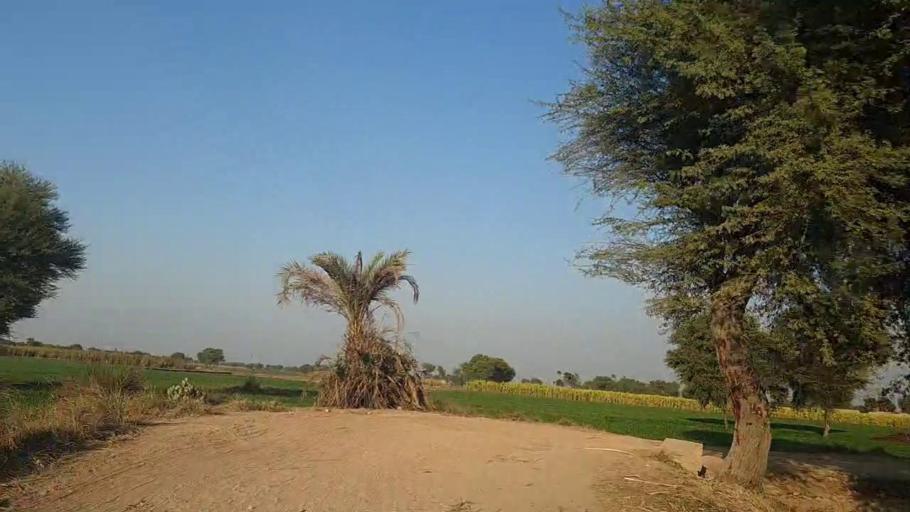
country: PK
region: Sindh
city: Sakrand
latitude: 26.2982
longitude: 68.1237
